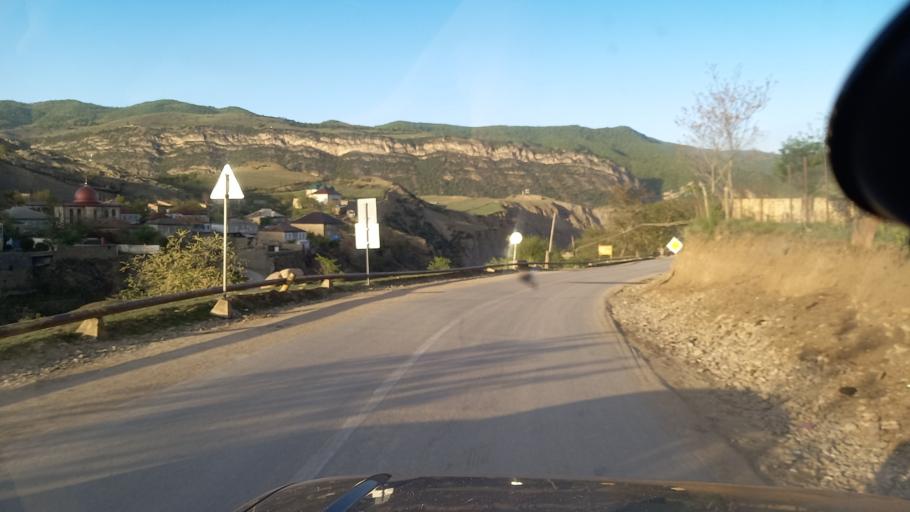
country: RU
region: Dagestan
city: Khuchni
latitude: 41.9747
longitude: 47.8947
